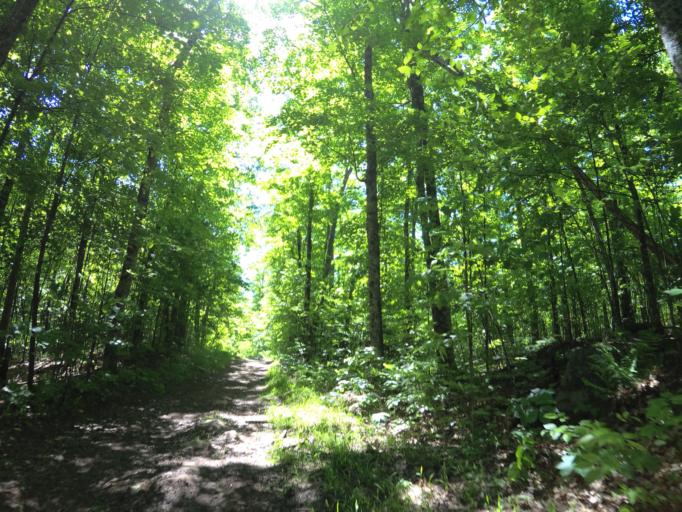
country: CA
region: Ontario
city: Renfrew
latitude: 45.0448
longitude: -77.0838
